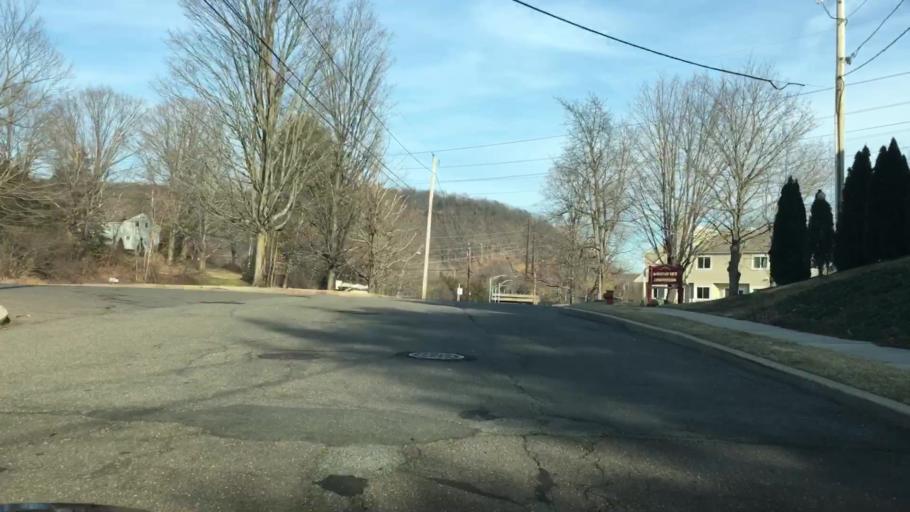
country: US
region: Connecticut
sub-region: New Haven County
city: Meriden
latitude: 41.5259
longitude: -72.7505
